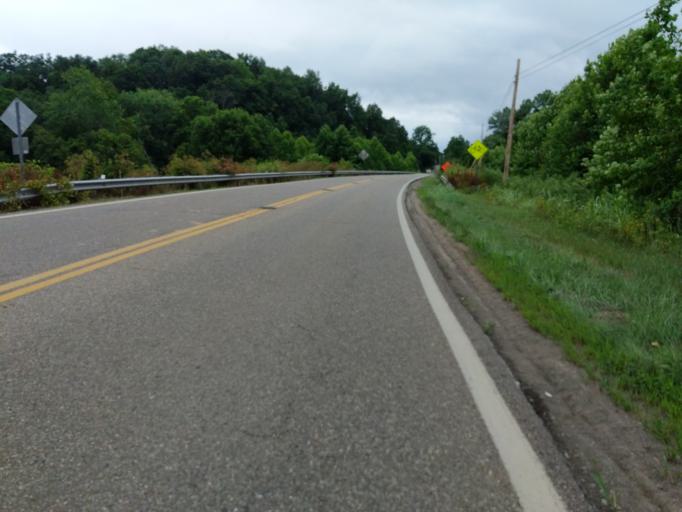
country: US
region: Ohio
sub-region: Athens County
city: Chauncey
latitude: 39.3895
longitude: -82.1420
